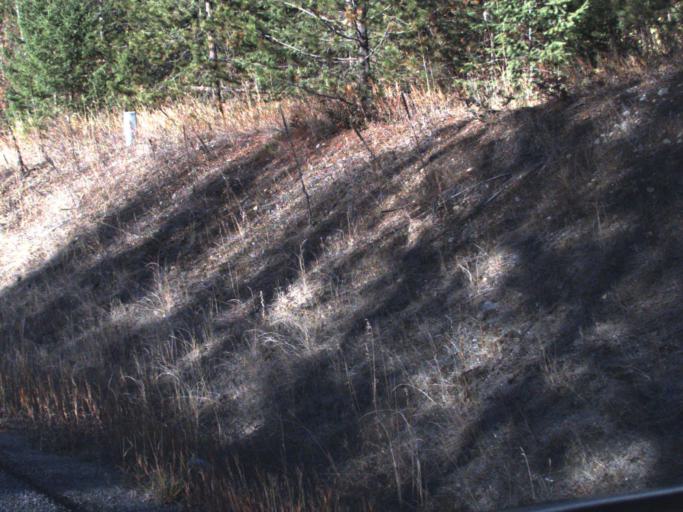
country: CA
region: British Columbia
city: Rossland
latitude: 48.9721
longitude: -117.8150
